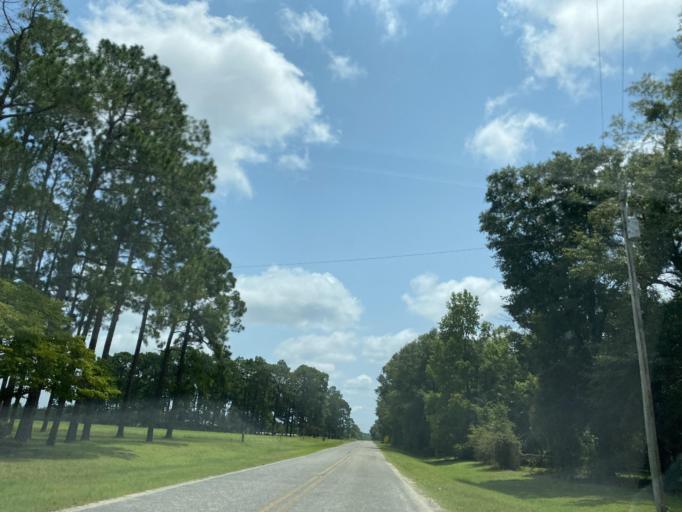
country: US
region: Georgia
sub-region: Telfair County
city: Lumber City
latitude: 32.0130
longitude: -82.7254
